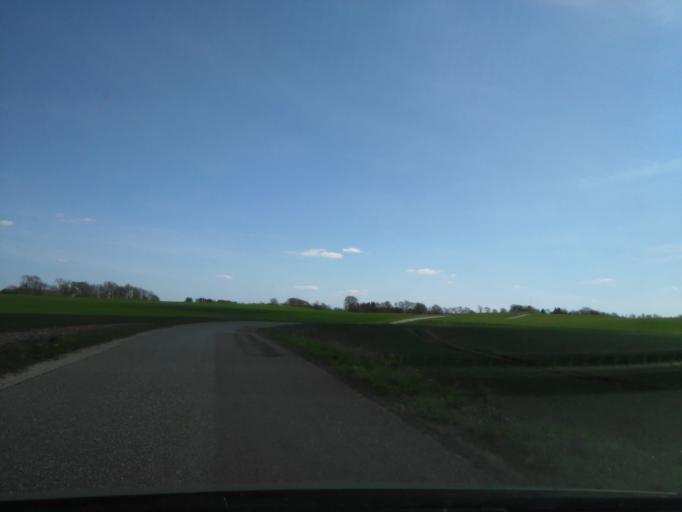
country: DK
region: Central Jutland
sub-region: Viborg Kommune
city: Viborg
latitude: 56.3583
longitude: 9.3376
